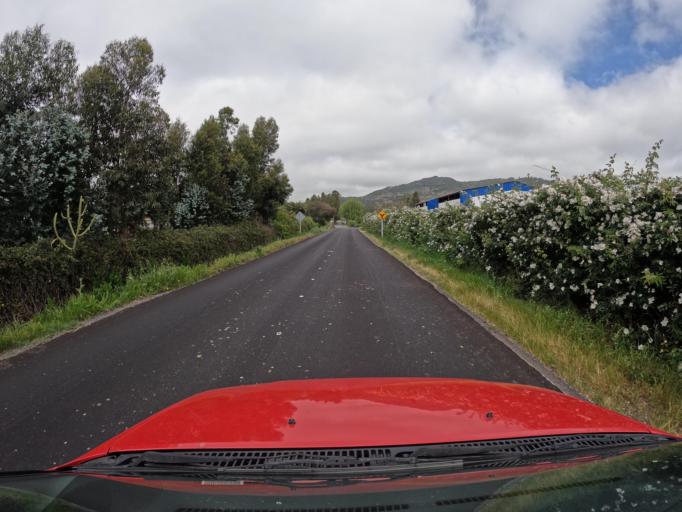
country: CL
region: O'Higgins
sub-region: Provincia de Colchagua
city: Santa Cruz
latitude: -34.6639
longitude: -71.3972
